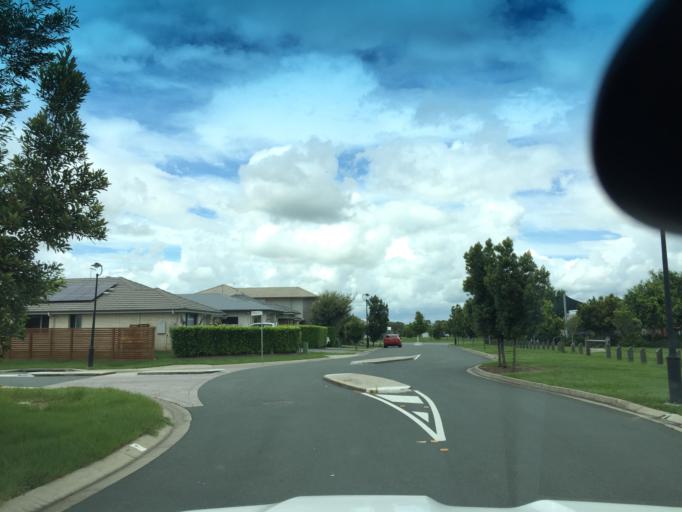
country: AU
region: Queensland
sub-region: Moreton Bay
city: Caboolture South
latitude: -27.0937
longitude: 152.9635
